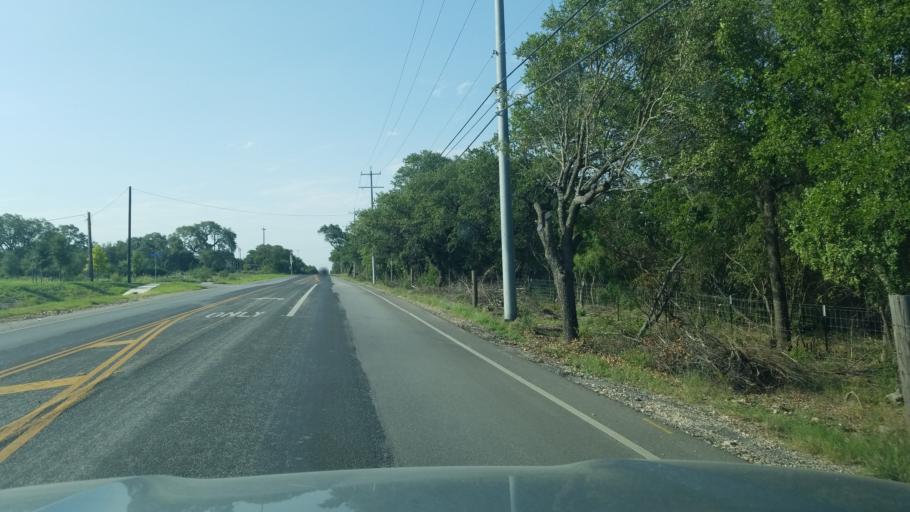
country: US
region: Texas
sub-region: Bexar County
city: Helotes
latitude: 29.4566
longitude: -98.7564
